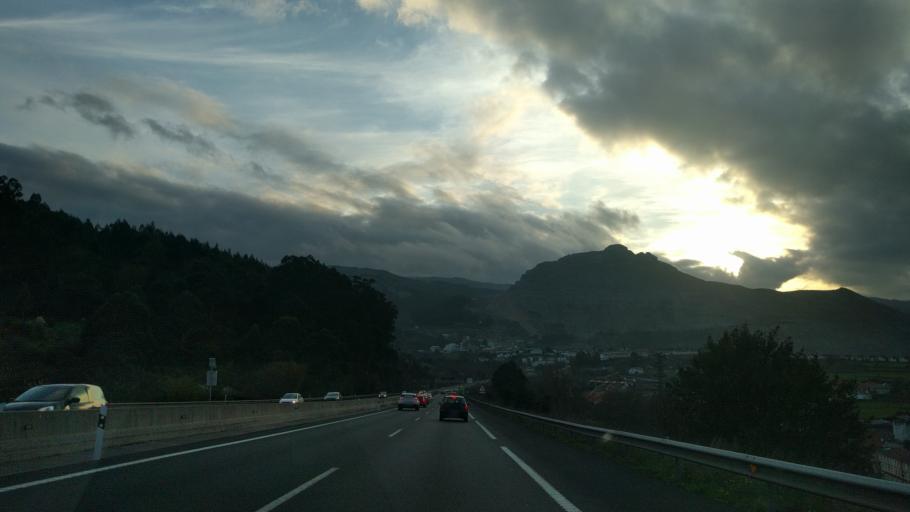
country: ES
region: Cantabria
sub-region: Provincia de Cantabria
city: Castro-Urdiales
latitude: 43.3566
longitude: -3.1989
